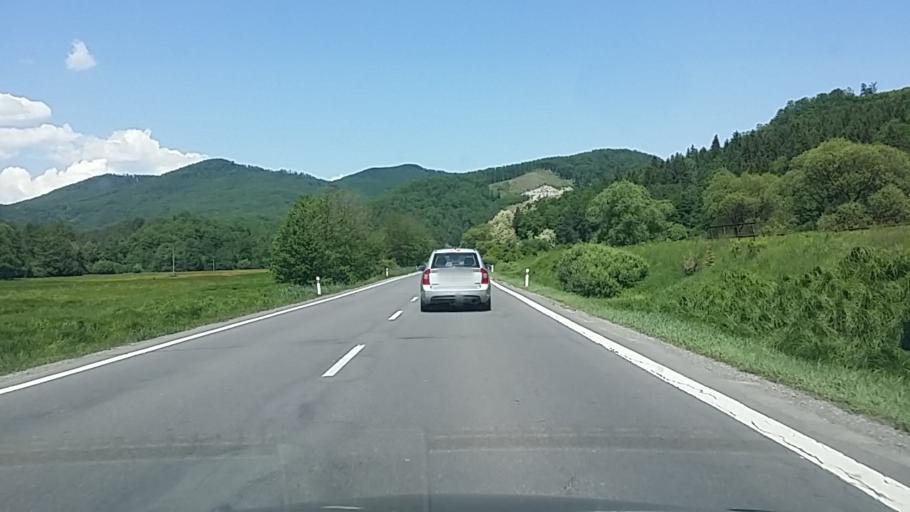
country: SK
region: Banskobystricky
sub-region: Okres Banska Bystrica
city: Zvolen
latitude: 48.5111
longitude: 19.0985
